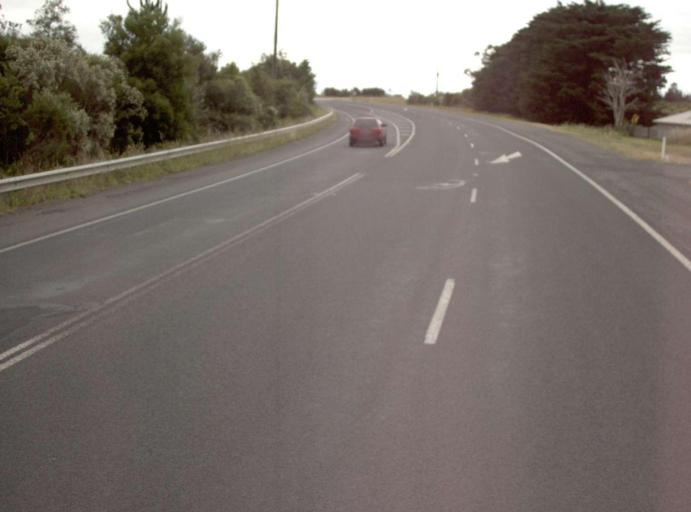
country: AU
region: Victoria
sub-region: Bass Coast
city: North Wonthaggi
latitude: -38.3910
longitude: 145.7487
